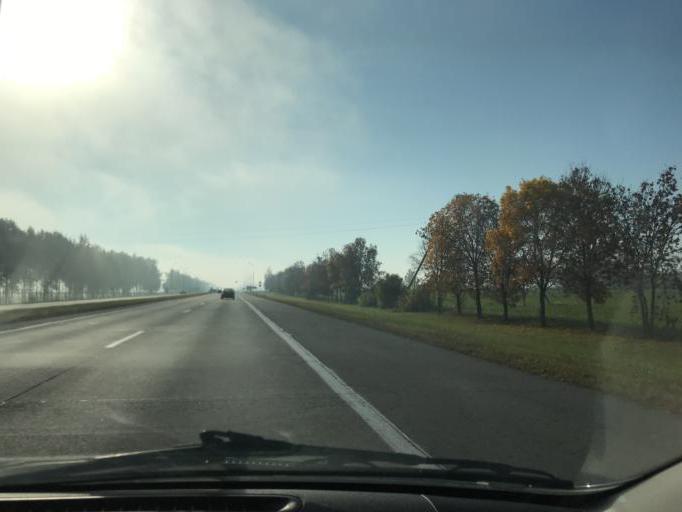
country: BY
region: Minsk
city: Samakhvalavichy
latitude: 53.5766
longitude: 27.4691
